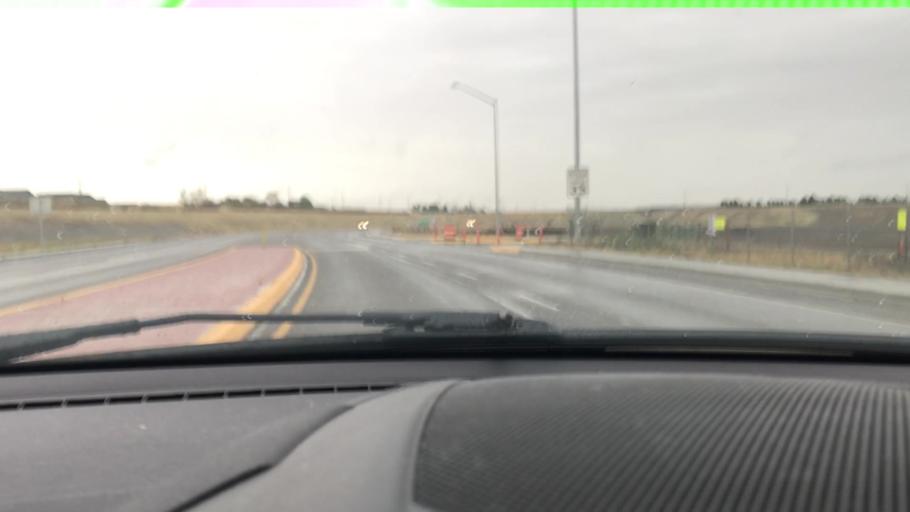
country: US
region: Montana
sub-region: Gallatin County
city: Belgrade
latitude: 45.7621
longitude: -111.1623
